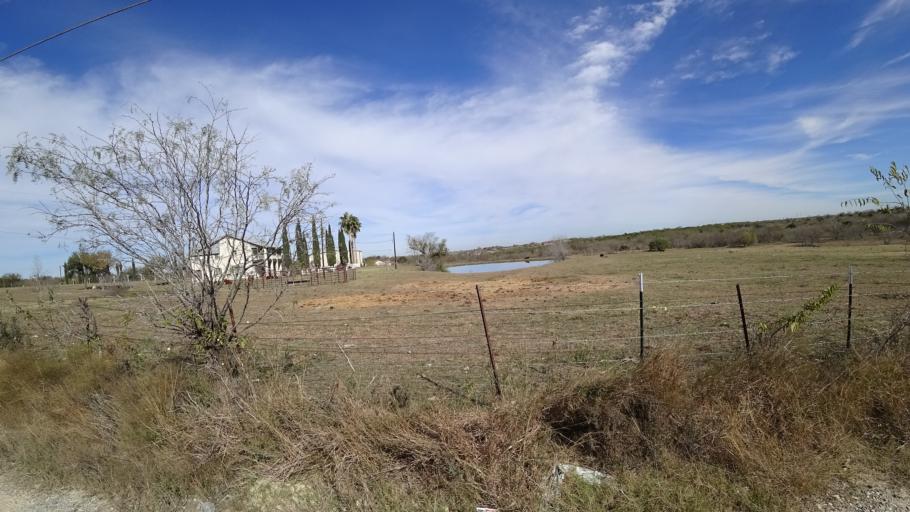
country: US
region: Texas
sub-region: Travis County
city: Onion Creek
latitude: 30.1189
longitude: -97.6889
